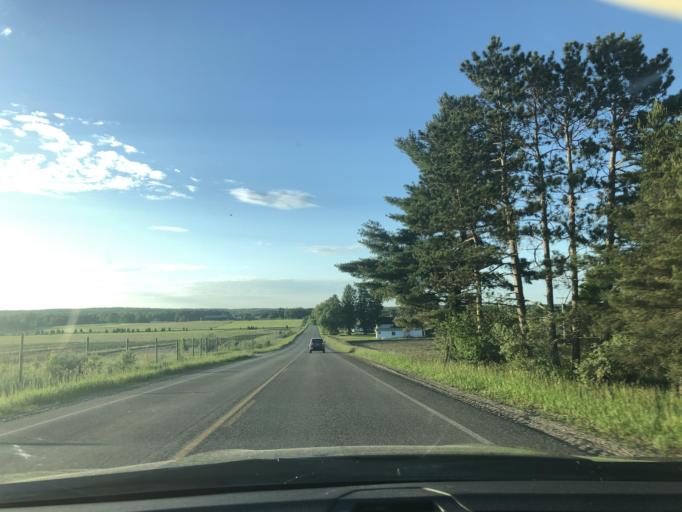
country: US
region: Michigan
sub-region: Missaukee County
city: Lake City
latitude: 44.4111
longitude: -85.0754
